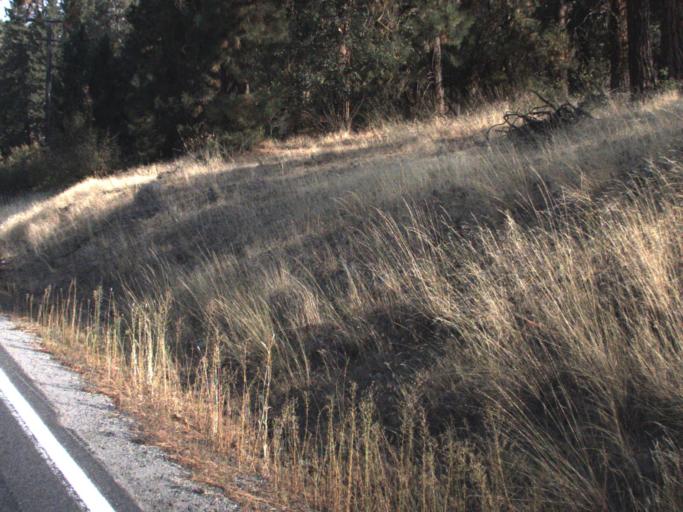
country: US
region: Washington
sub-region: Spokane County
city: Fairwood
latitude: 47.7941
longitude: -117.5320
